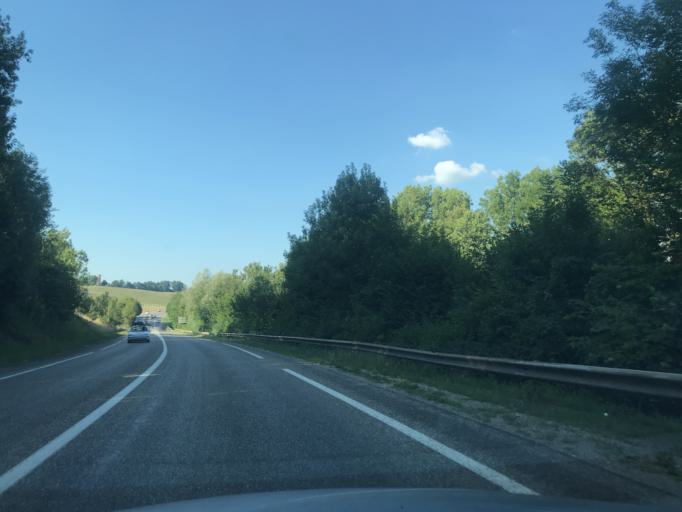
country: FR
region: Rhone-Alpes
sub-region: Departement de la Haute-Savoie
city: Seynod
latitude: 45.8676
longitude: 6.0727
